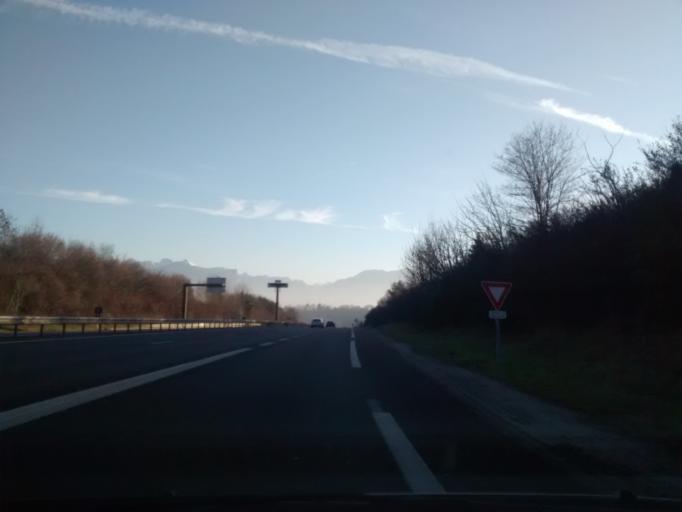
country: FR
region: Rhone-Alpes
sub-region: Departement de la Haute-Savoie
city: Lucinges
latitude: 46.1807
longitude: 6.3058
